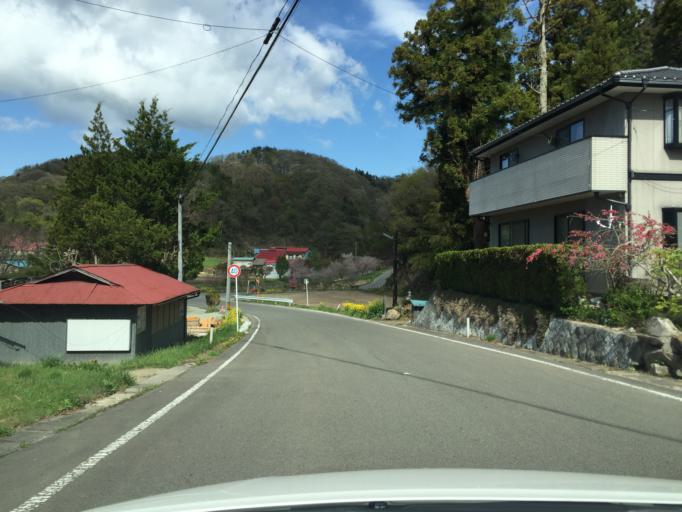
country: JP
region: Fukushima
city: Funehikimachi-funehiki
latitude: 37.5598
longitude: 140.6601
